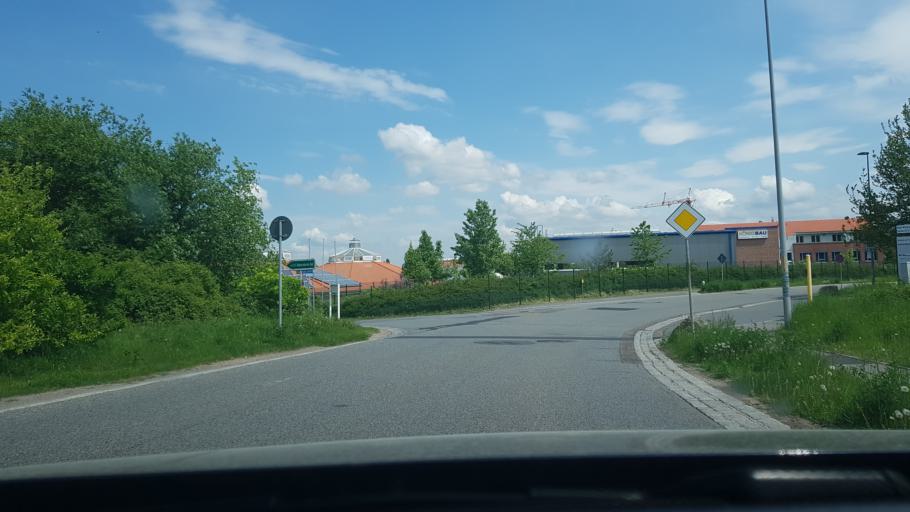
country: DE
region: Saxony
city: Tharandt
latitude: 51.0363
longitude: 13.5862
